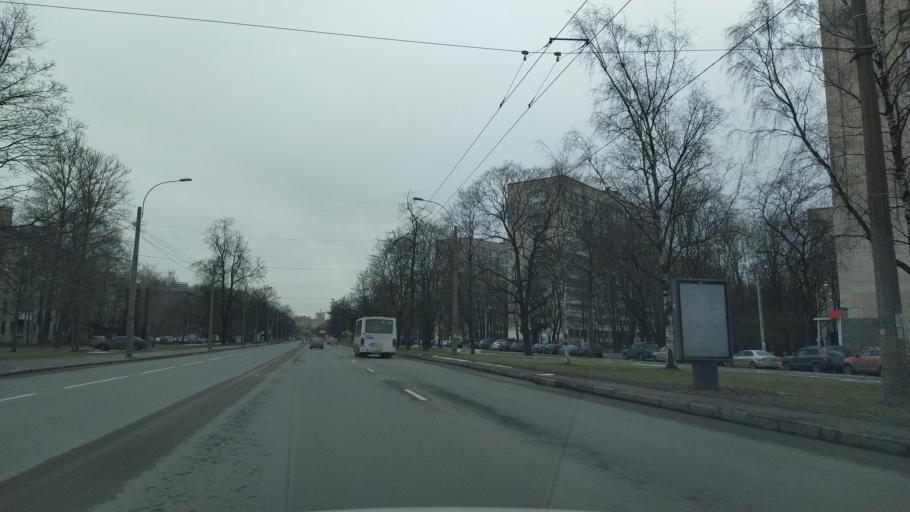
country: RU
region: St.-Petersburg
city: Kushelevka
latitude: 60.0039
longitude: 30.3579
